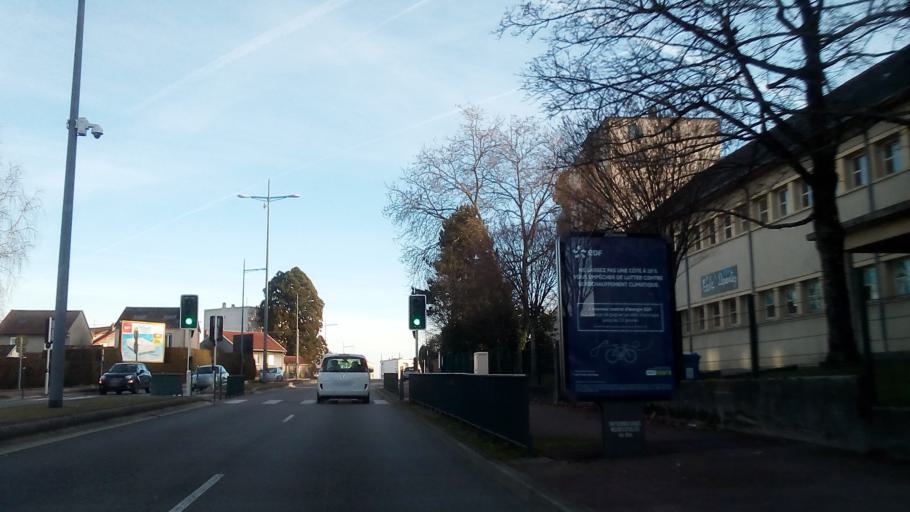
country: FR
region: Limousin
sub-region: Departement de la Haute-Vienne
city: Limoges
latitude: 45.8497
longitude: 1.2476
